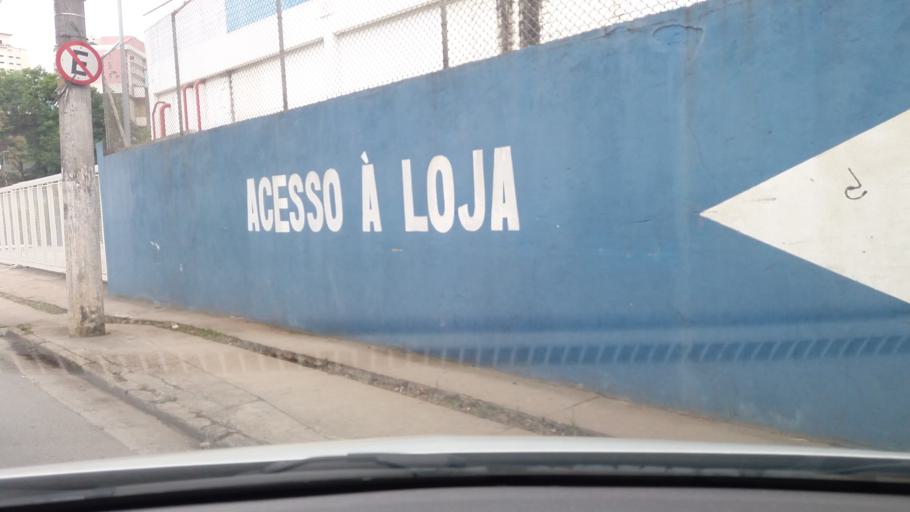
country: BR
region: Sao Paulo
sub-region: Taboao Da Serra
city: Taboao da Serra
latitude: -23.6113
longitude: -46.7038
